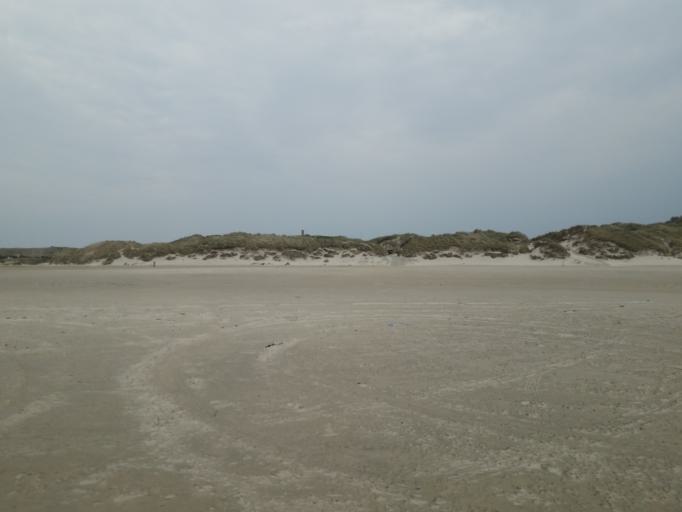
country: DK
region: North Denmark
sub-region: Jammerbugt Kommune
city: Pandrup
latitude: 57.2688
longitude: 9.5940
